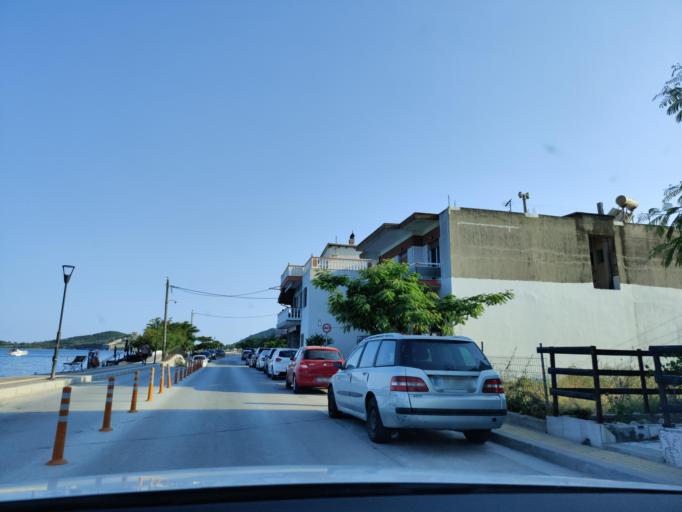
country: GR
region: East Macedonia and Thrace
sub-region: Nomos Kavalas
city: Nea Peramos
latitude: 40.8365
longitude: 24.3053
